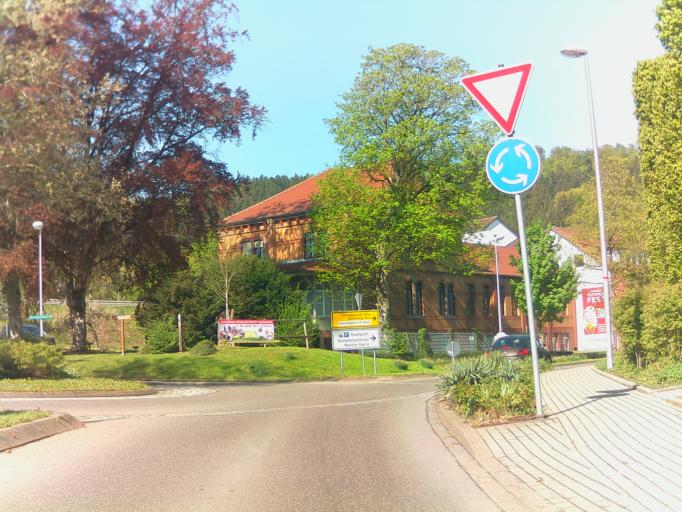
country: DE
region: Baden-Wuerttemberg
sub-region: Karlsruhe Region
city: Nagold
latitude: 48.5474
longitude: 8.7174
